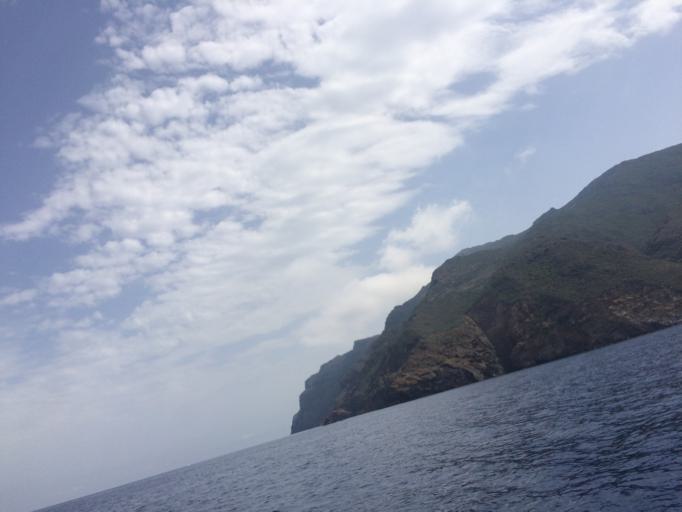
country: IT
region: Tuscany
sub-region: Provincia di Livorno
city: Capraia Isola
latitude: 43.0506
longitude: 9.7943
